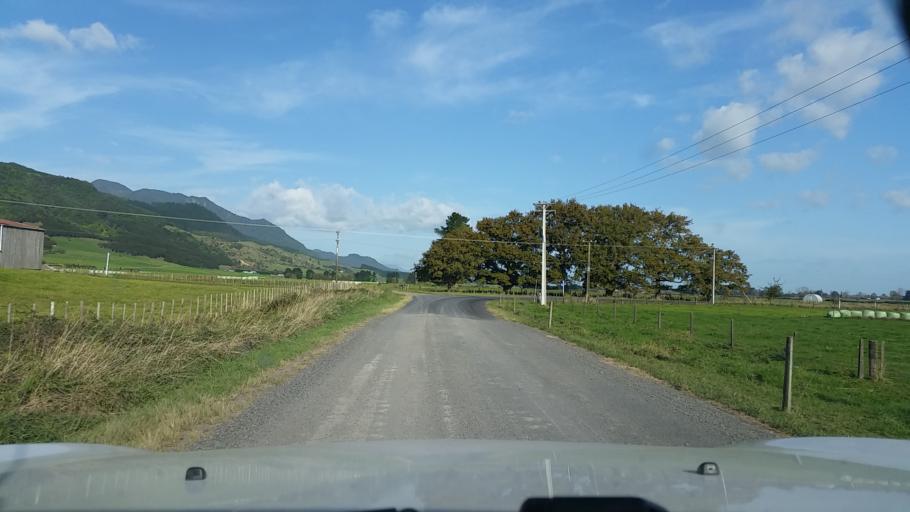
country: NZ
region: Bay of Plenty
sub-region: Western Bay of Plenty District
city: Katikati
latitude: -37.6149
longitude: 175.7959
